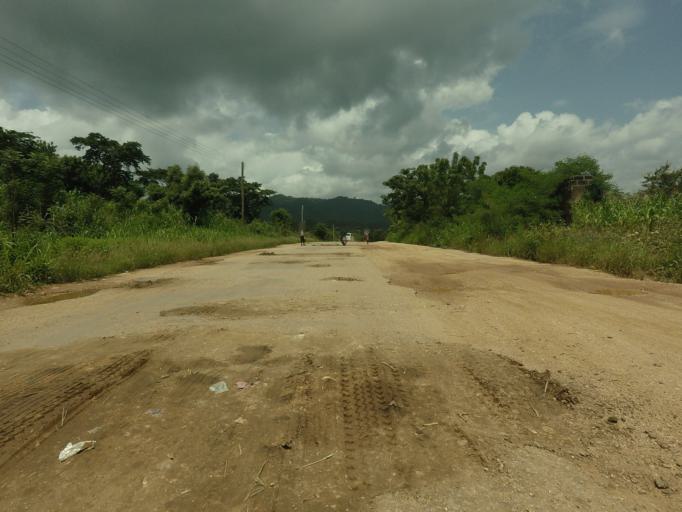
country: GH
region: Volta
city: Ho
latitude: 6.6989
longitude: 0.3352
